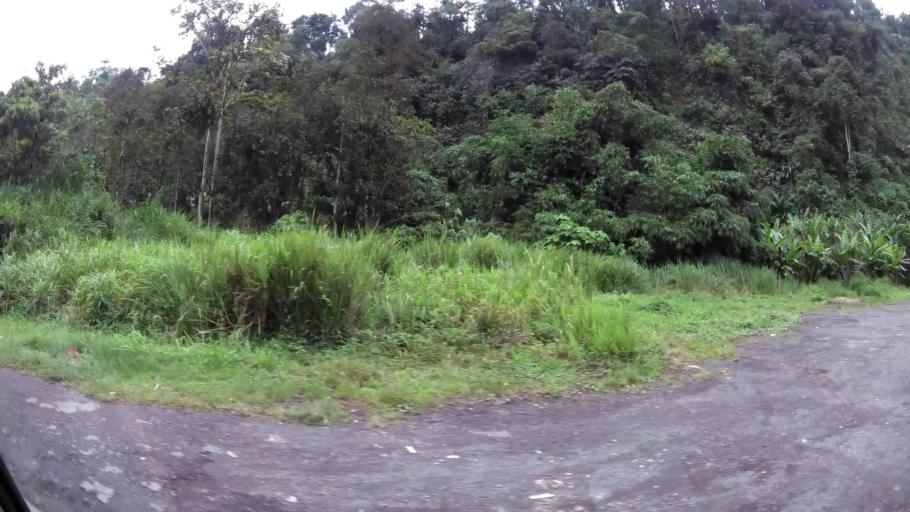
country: EC
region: Santo Domingo de los Tsachilas
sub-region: Canton Santo Domingo de los Colorados
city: Santo Domingo de los Colorados
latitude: -0.2688
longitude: -79.0851
